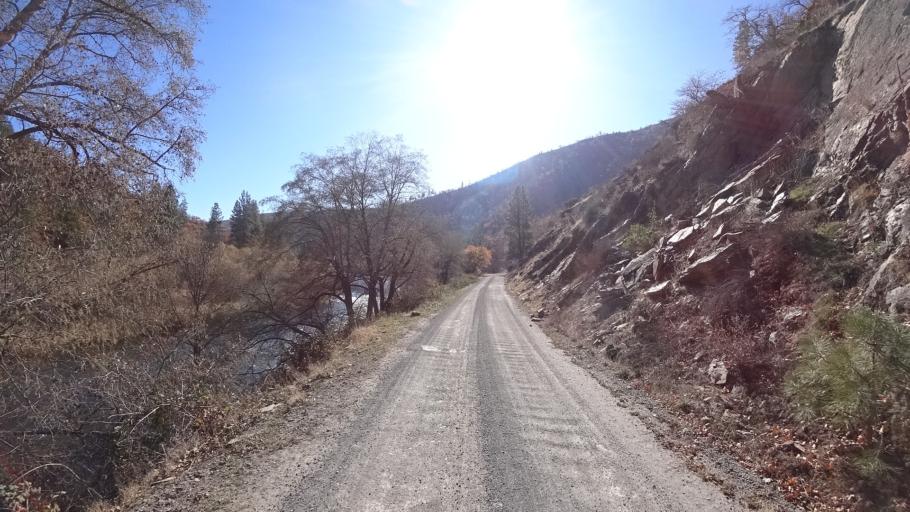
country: US
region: California
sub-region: Siskiyou County
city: Yreka
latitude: 41.8453
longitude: -122.6848
